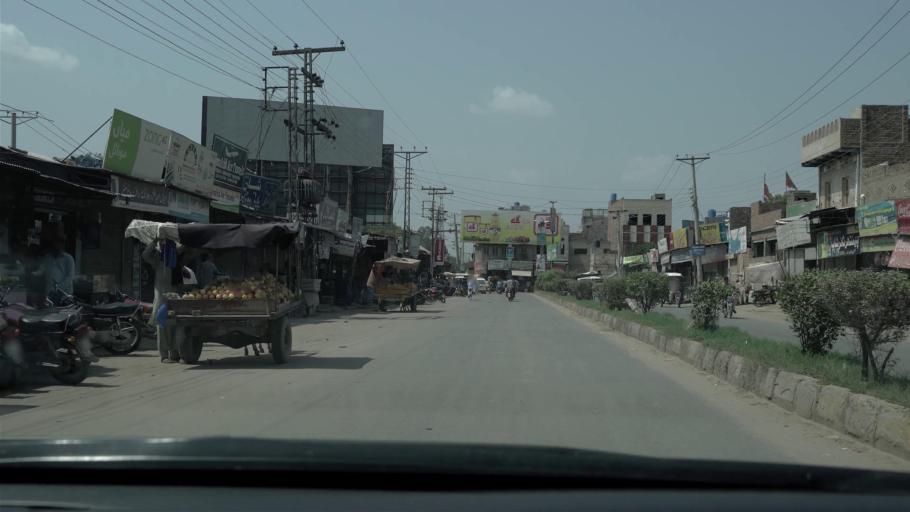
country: PK
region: Punjab
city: Gojra
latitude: 31.1513
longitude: 72.6788
